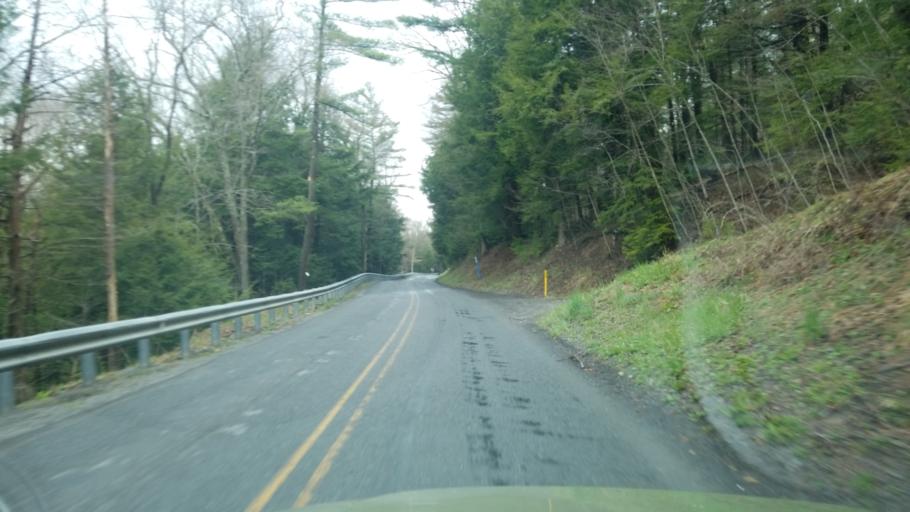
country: US
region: Pennsylvania
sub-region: Clearfield County
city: Clearfield
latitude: 41.0656
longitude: -78.4192
